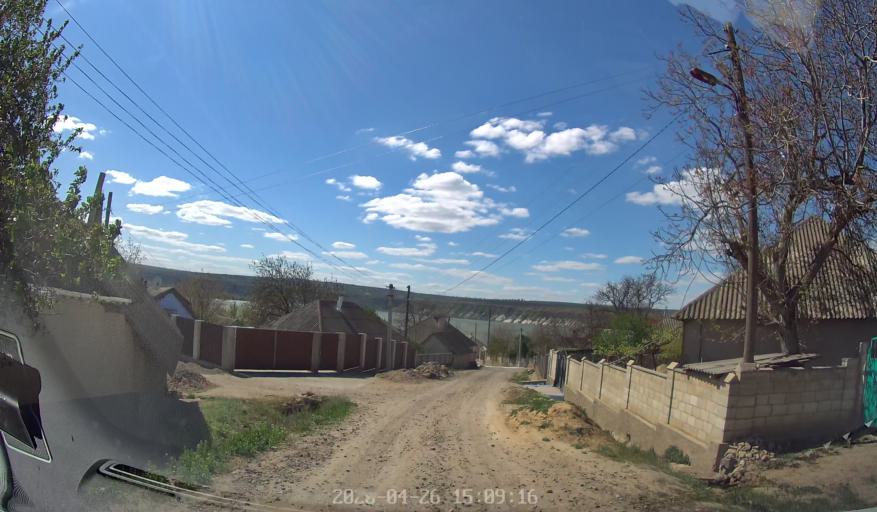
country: MD
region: Telenesti
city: Cocieri
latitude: 47.3554
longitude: 29.1078
